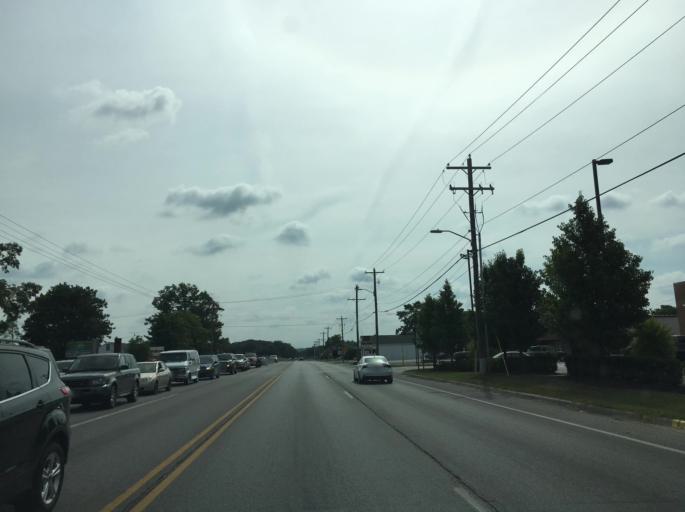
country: US
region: Michigan
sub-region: Grand Traverse County
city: Traverse City
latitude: 44.7333
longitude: -85.5947
